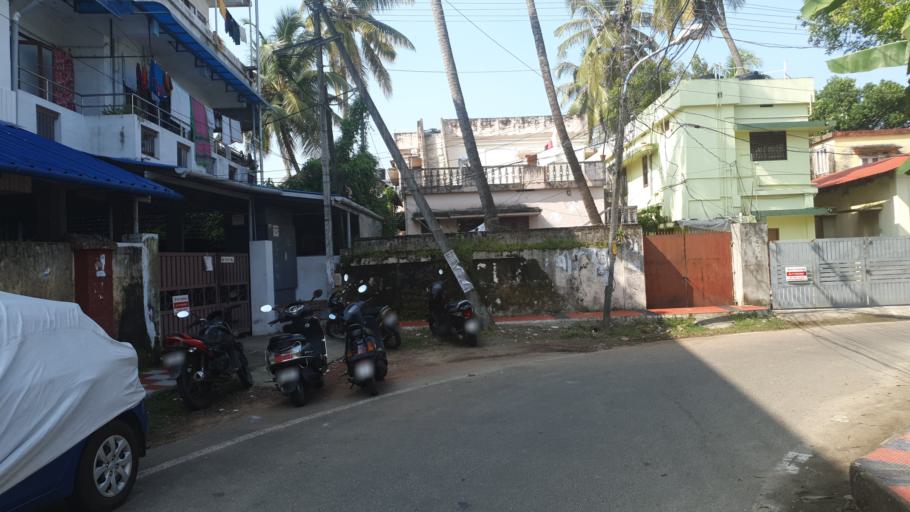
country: IN
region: Kerala
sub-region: Ernakulam
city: Cochin
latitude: 9.9608
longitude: 76.2558
